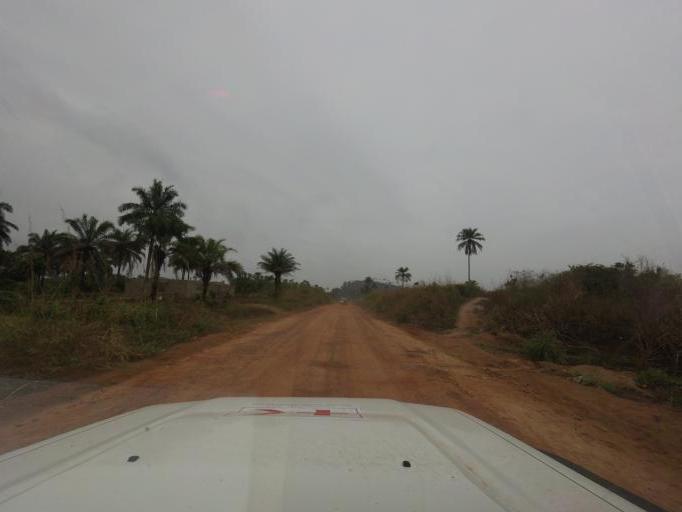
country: LR
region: Lofa
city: Voinjama
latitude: 8.4121
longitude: -9.7720
